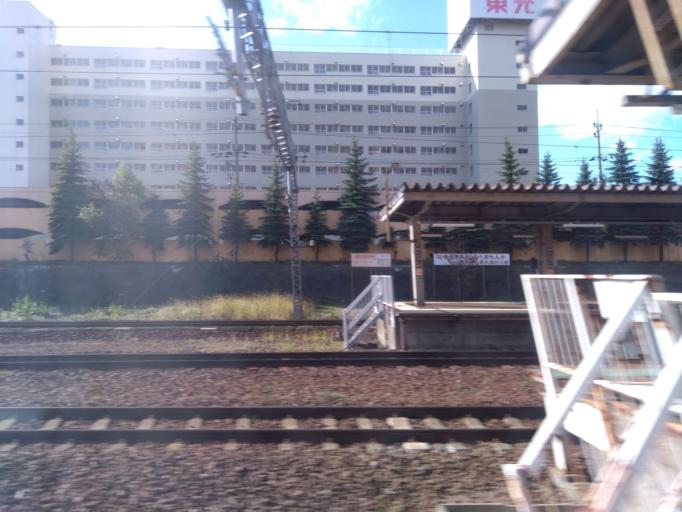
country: JP
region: Hokkaido
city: Kitahiroshima
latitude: 42.9780
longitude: 141.5635
